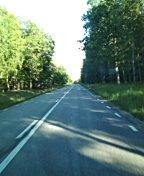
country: SE
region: Uppsala
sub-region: Habo Kommun
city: Balsta
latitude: 59.6463
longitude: 17.4300
